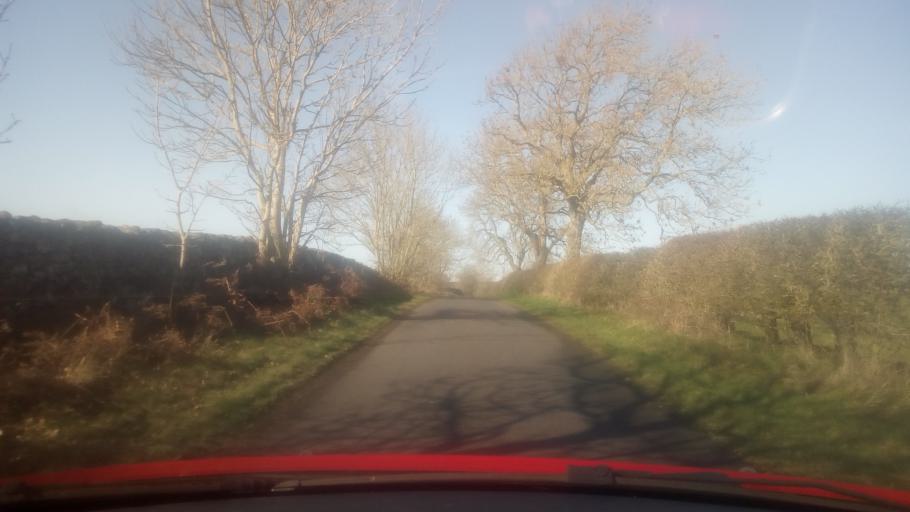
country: GB
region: Scotland
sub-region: The Scottish Borders
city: Jedburgh
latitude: 55.5215
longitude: -2.5999
